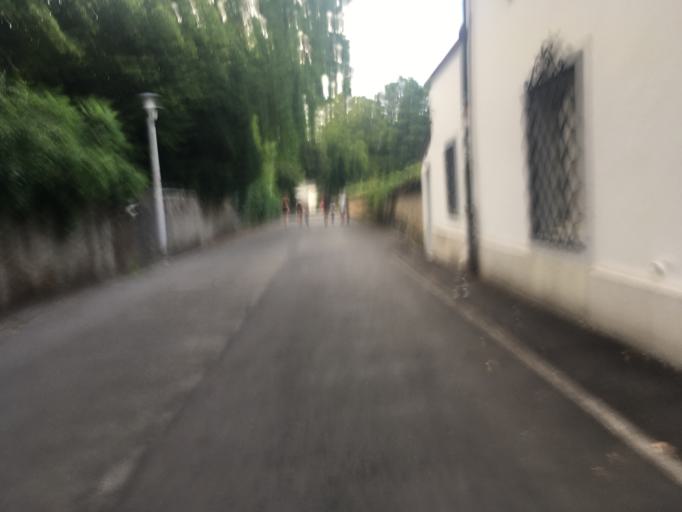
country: CH
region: Solothurn
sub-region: Bezirk Solothurn
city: Solothurn
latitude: 47.2030
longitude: 7.5320
